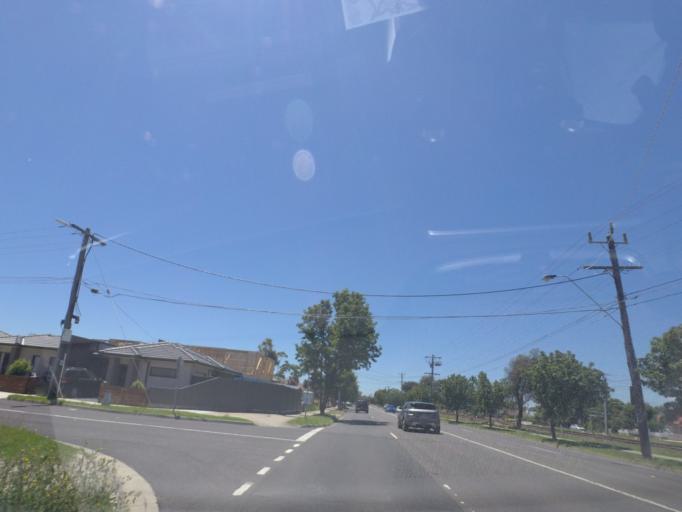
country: AU
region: Victoria
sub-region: Whittlesea
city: Lalor
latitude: -37.6704
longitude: 145.0156
